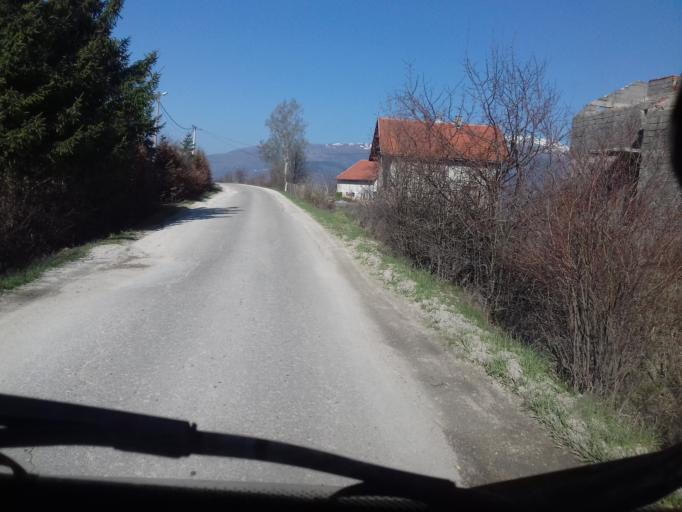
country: BA
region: Federation of Bosnia and Herzegovina
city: Lokvine
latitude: 44.2431
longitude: 17.7882
